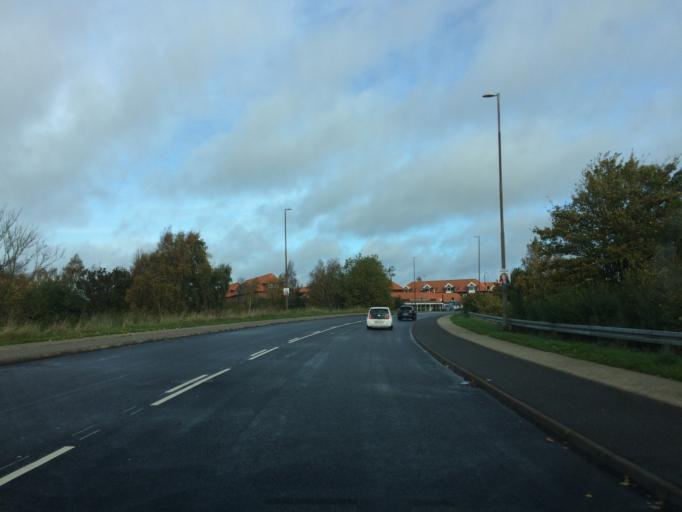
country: DK
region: South Denmark
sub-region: Fredericia Kommune
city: Fredericia
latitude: 55.5731
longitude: 9.7426
